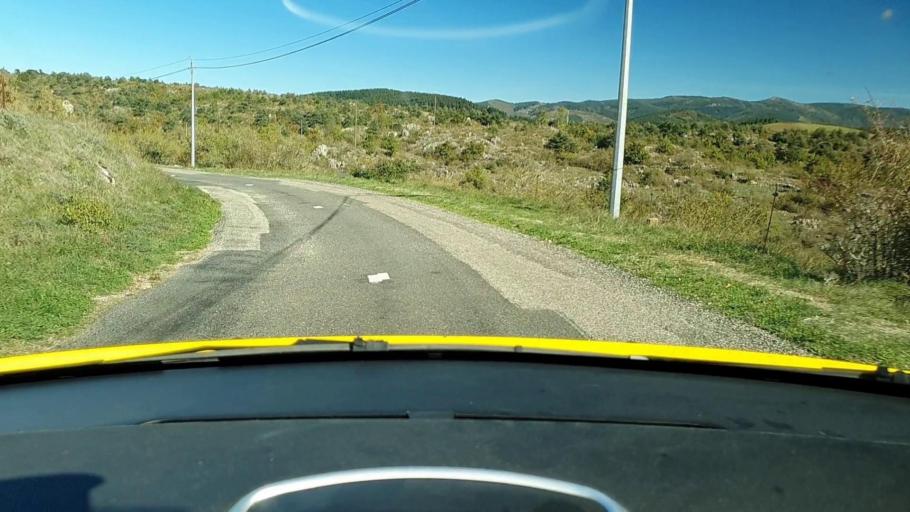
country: FR
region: Languedoc-Roussillon
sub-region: Departement du Gard
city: Aveze
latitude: 43.9606
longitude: 3.3921
